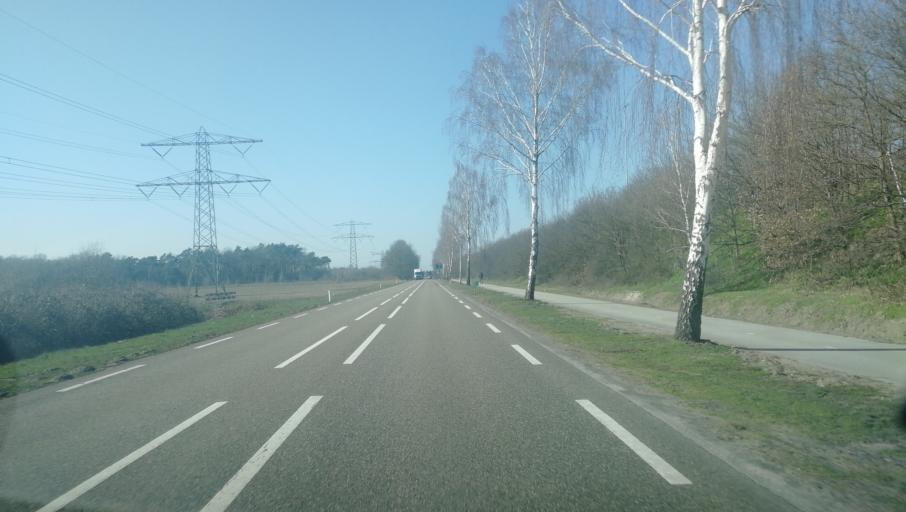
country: NL
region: Limburg
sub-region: Gemeente Venlo
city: Tegelen
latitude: 51.3896
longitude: 6.1061
